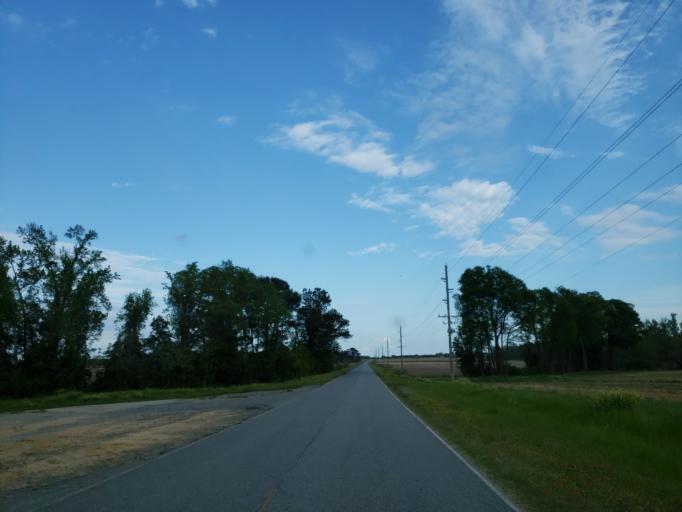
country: US
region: Georgia
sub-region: Dooly County
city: Vienna
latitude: 32.1235
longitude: -83.7126
